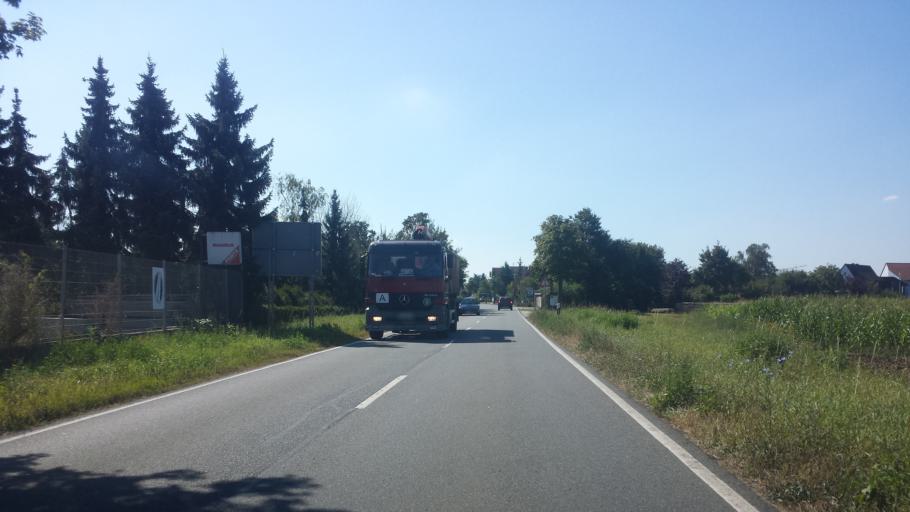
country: DE
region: Hesse
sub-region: Regierungsbezirk Darmstadt
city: Einhausen
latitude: 49.6767
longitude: 8.5520
